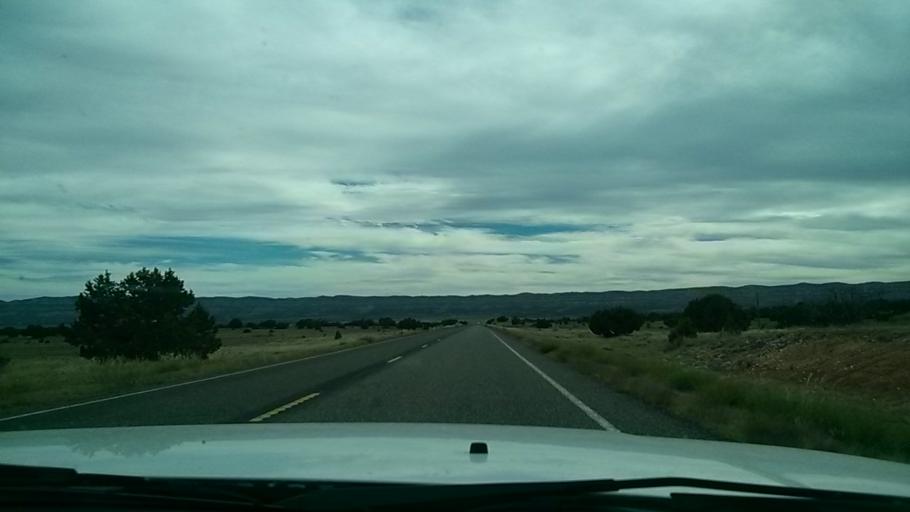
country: US
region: Utah
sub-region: Wayne County
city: Loa
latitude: 37.7382
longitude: -111.5080
